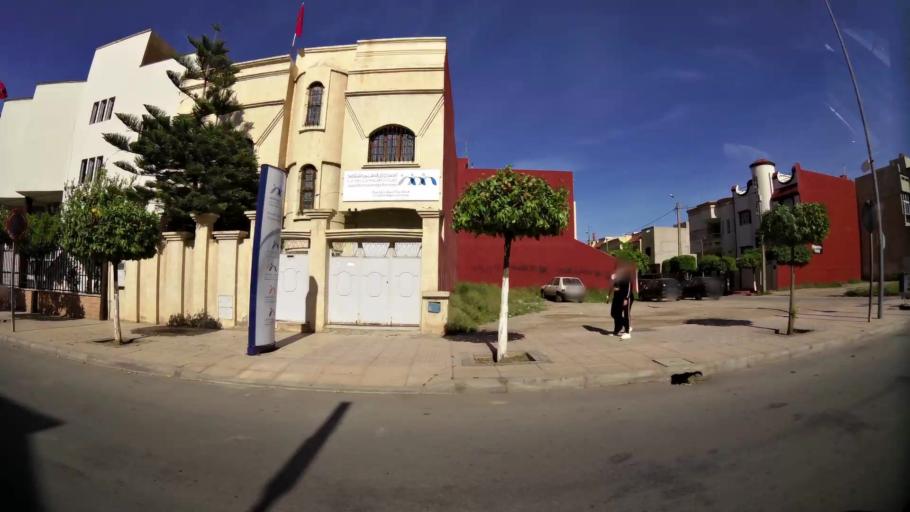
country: MA
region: Oriental
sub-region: Oujda-Angad
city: Oujda
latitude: 34.6660
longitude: -1.9065
